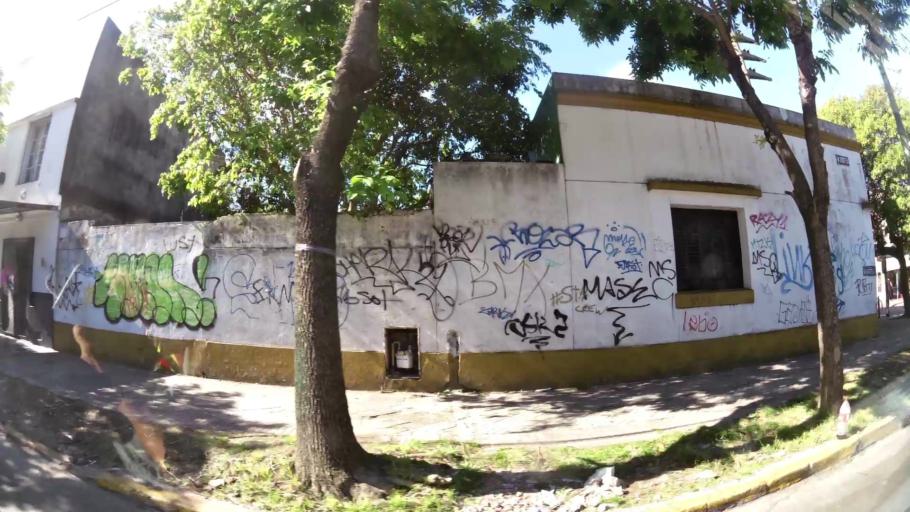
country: AR
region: Buenos Aires
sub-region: Partido de Lomas de Zamora
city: Lomas de Zamora
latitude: -34.7679
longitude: -58.4105
